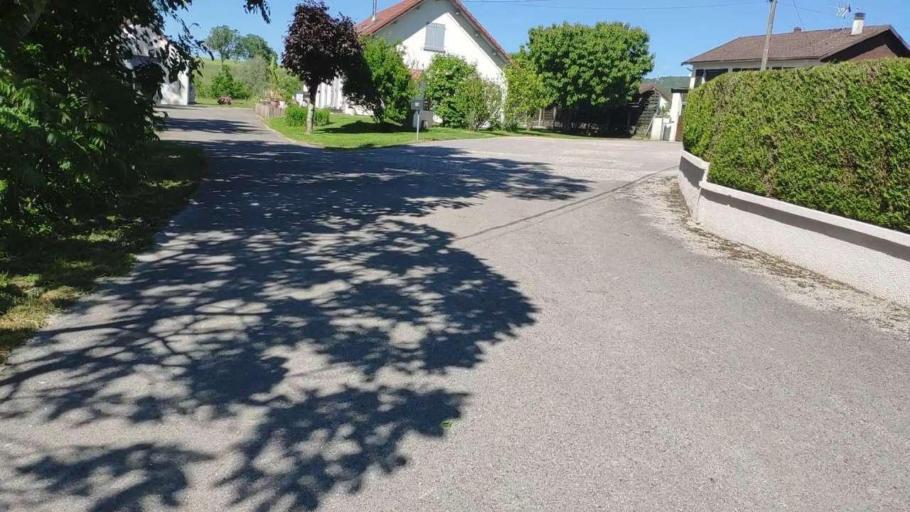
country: FR
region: Franche-Comte
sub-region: Departement du Jura
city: Perrigny
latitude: 46.7317
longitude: 5.5831
